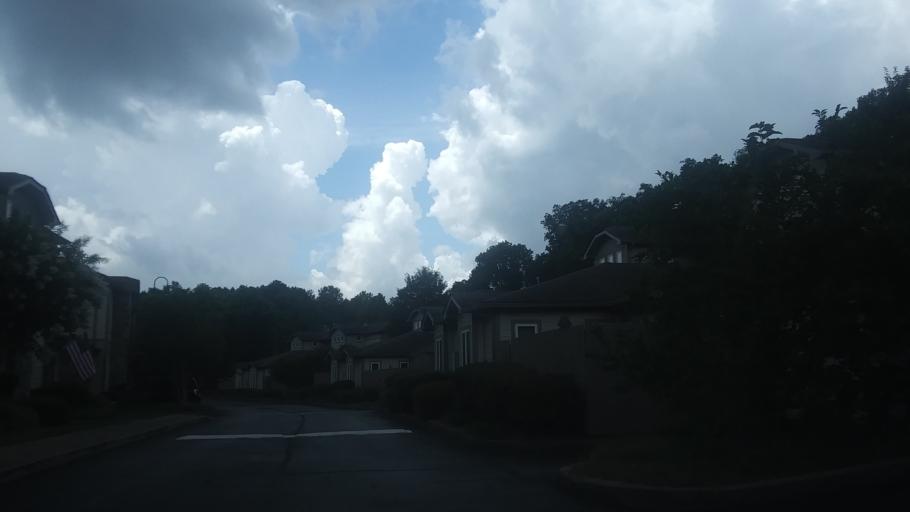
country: US
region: Tennessee
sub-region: Davidson County
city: Belle Meade
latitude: 36.0887
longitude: -86.9170
